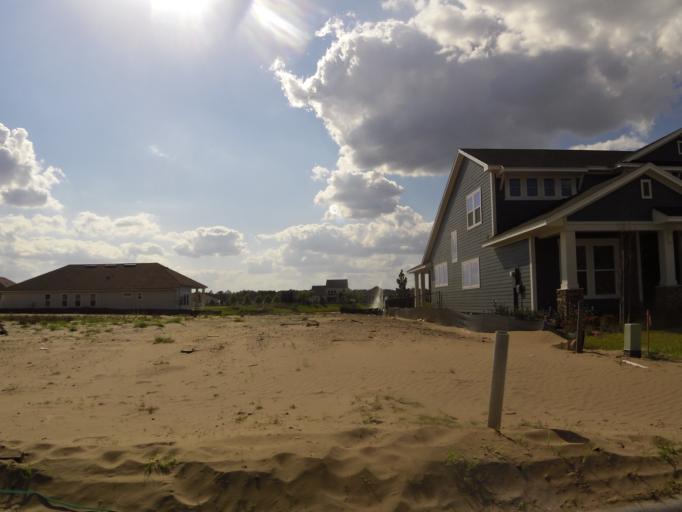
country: US
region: Florida
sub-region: Saint Johns County
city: Palm Valley
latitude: 30.1745
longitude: -81.5029
